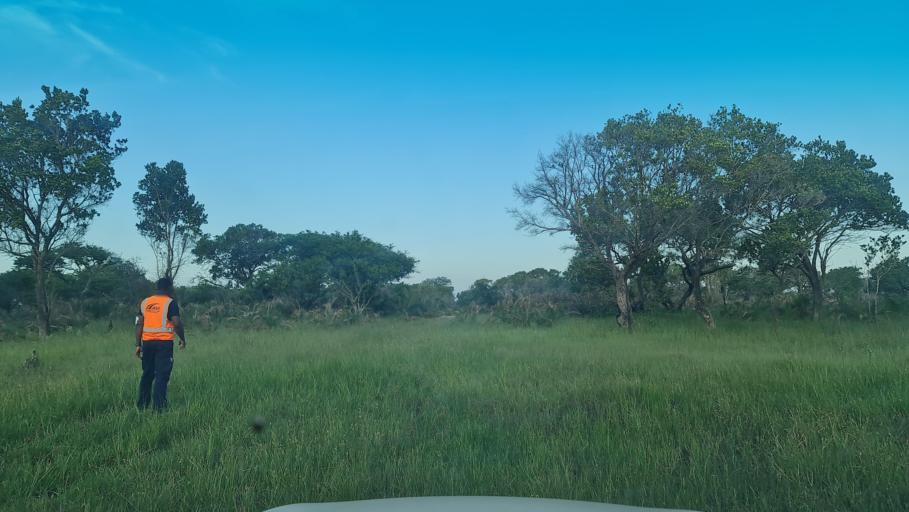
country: MZ
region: Gaza
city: Macia
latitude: -25.2175
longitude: 33.0466
